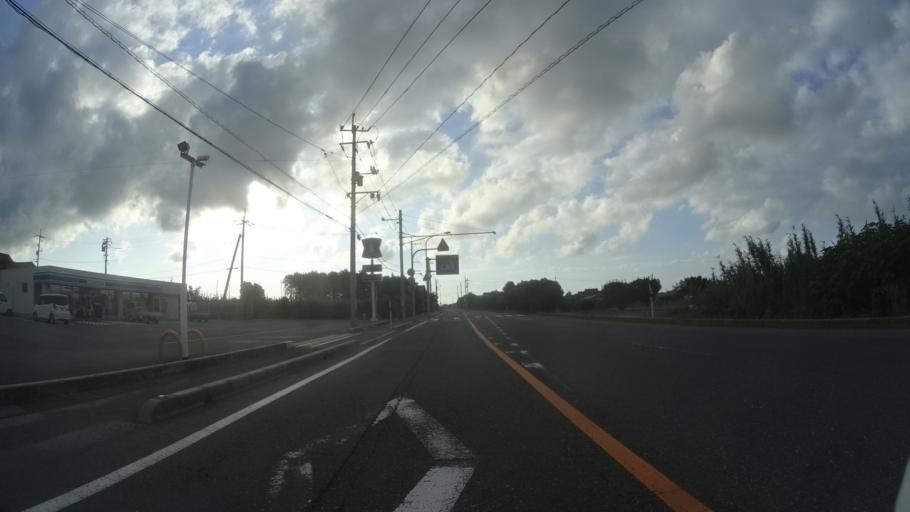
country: JP
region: Tottori
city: Kurayoshi
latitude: 35.5217
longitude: 133.5989
